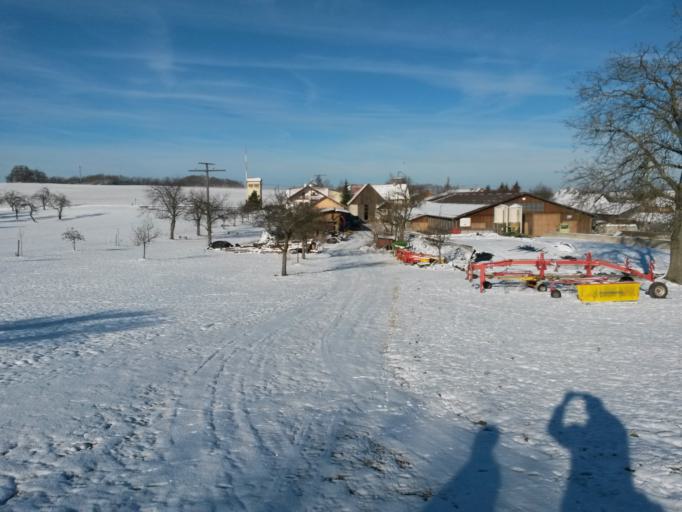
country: DE
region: Baden-Wuerttemberg
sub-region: Regierungsbezirk Stuttgart
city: Bad Uberkingen
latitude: 48.6155
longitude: 9.7811
